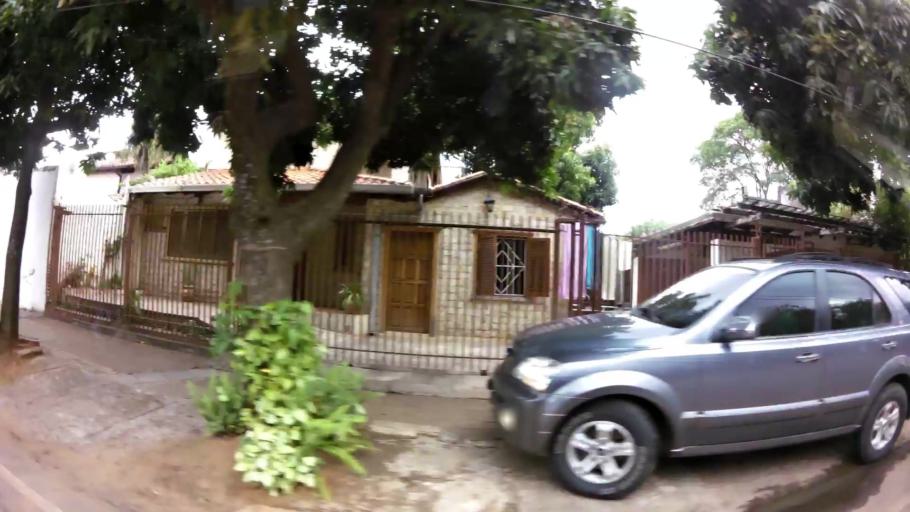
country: PY
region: Central
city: Fernando de la Mora
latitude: -25.3287
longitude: -57.5513
